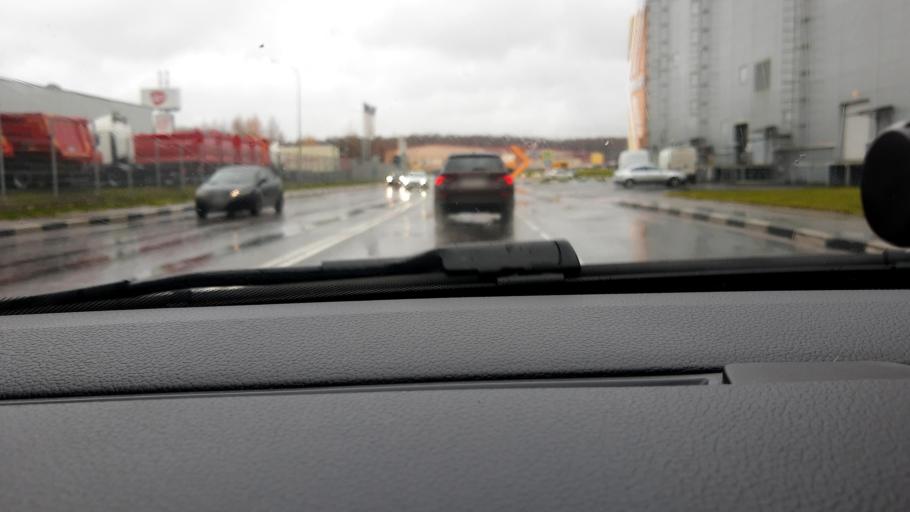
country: RU
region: Moscow
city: Lianozovo
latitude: 55.9134
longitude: 37.5872
